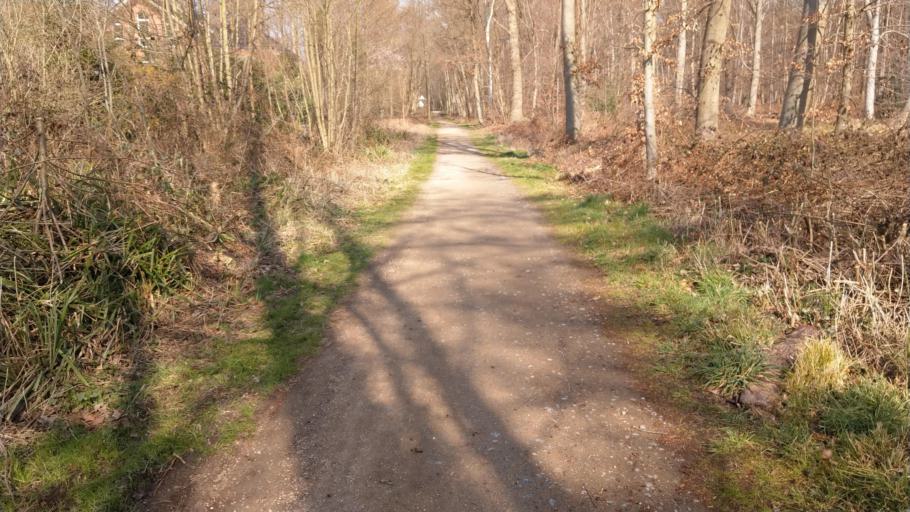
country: DE
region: North Rhine-Westphalia
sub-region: Regierungsbezirk Koln
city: Wassenberg
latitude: 51.1063
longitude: 6.1595
